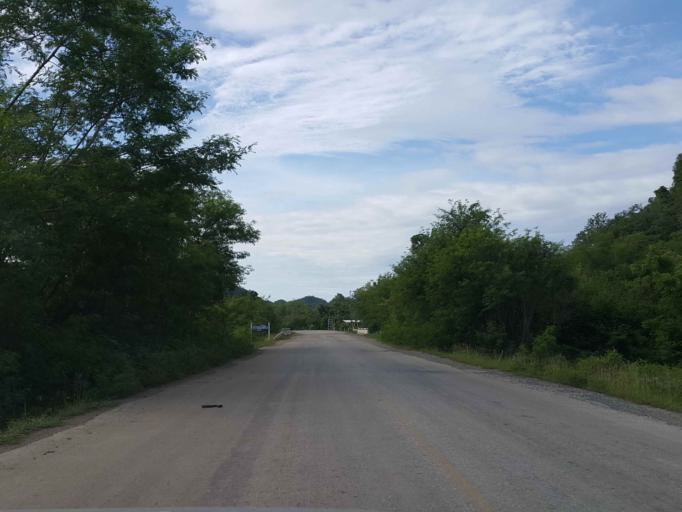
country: TH
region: Sukhothai
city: Thung Saliam
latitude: 17.2739
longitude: 99.5309
